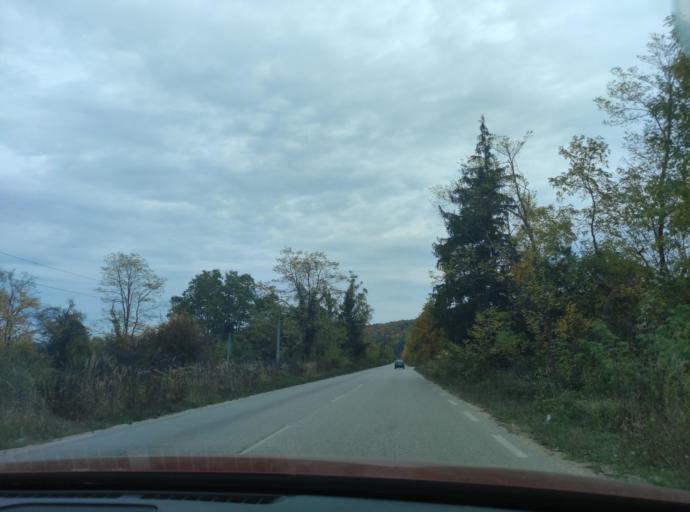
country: BG
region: Montana
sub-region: Obshtina Berkovitsa
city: Berkovitsa
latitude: 43.2554
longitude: 23.1722
